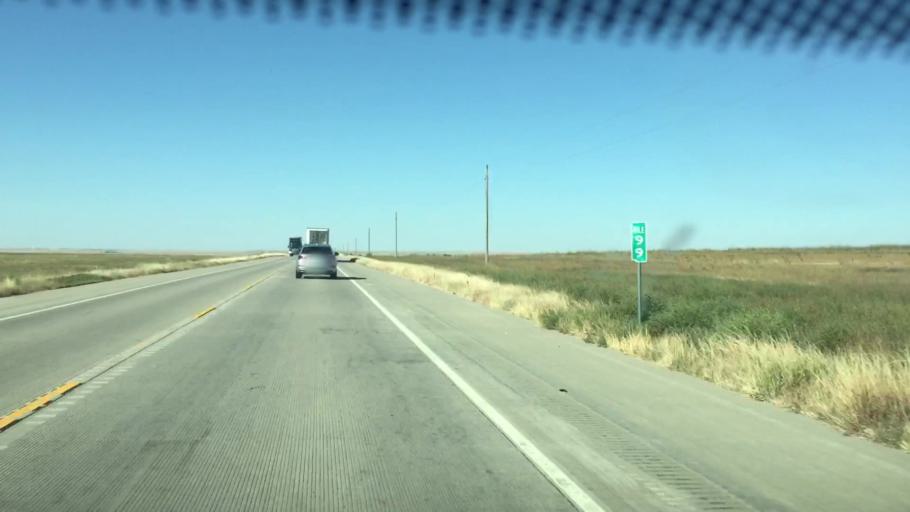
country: US
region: Colorado
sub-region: Kiowa County
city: Eads
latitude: 38.3104
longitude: -102.7199
